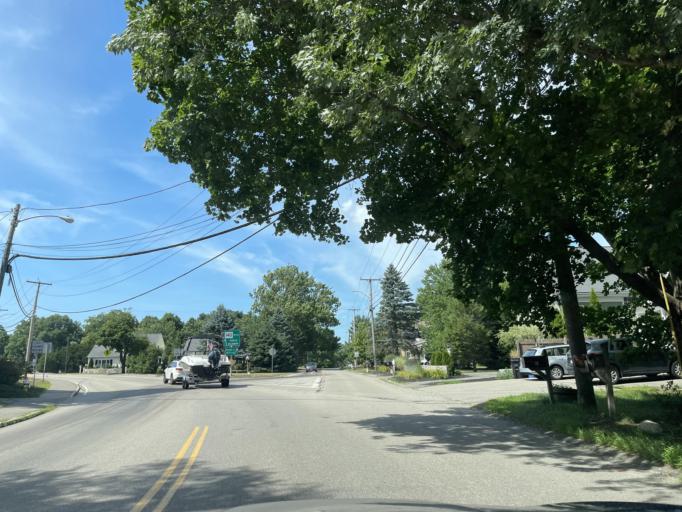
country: US
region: Massachusetts
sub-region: Norfolk County
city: Wrentham
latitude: 42.0724
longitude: -71.3294
